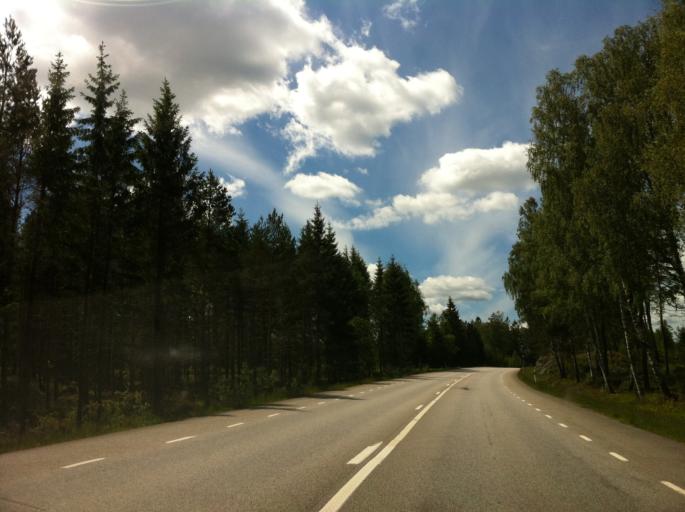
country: SE
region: Vaestra Goetaland
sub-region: Amals Kommun
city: Amal
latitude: 58.9921
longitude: 12.6724
